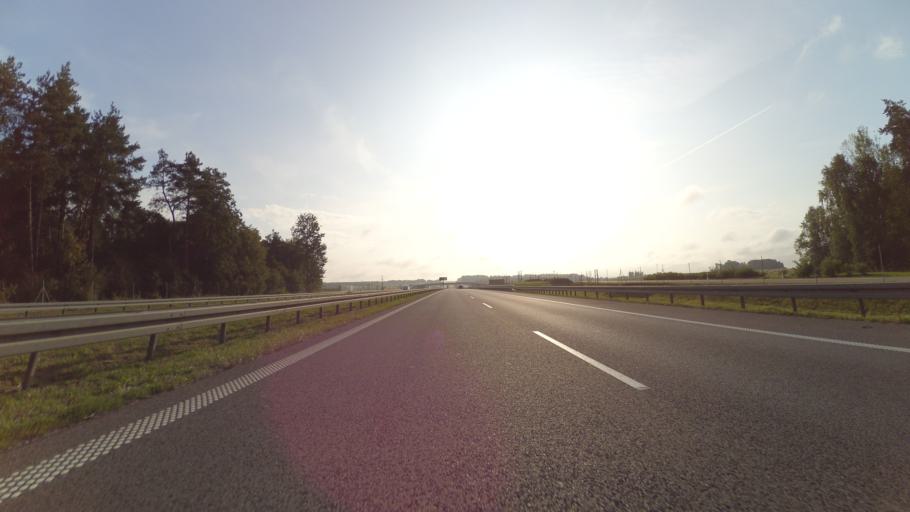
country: PL
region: Podlasie
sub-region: Powiat bialostocki
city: Tykocin
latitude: 53.1399
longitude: 22.7710
